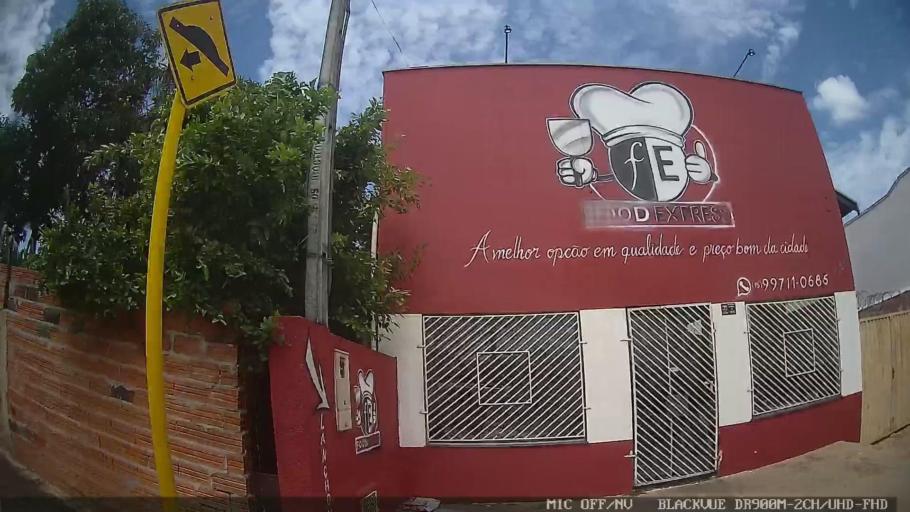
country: BR
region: Sao Paulo
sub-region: Laranjal Paulista
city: Laranjal Paulista
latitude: -23.0405
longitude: -47.8228
